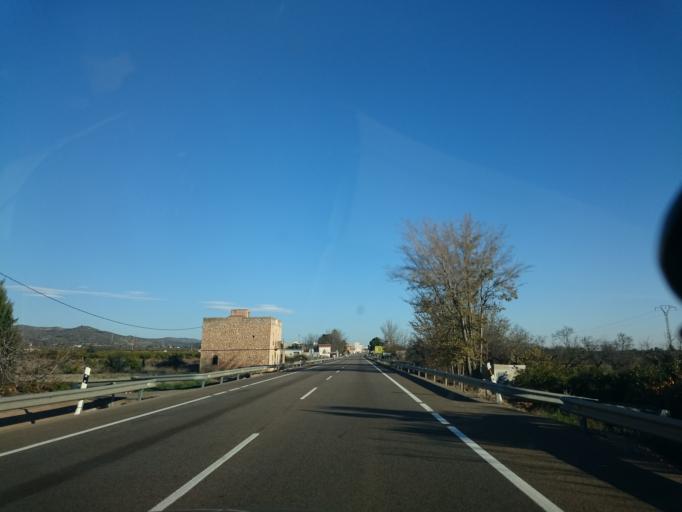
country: ES
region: Valencia
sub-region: Provincia de Castello
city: Orpesa/Oropesa del Mar
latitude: 40.1471
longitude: 0.1555
